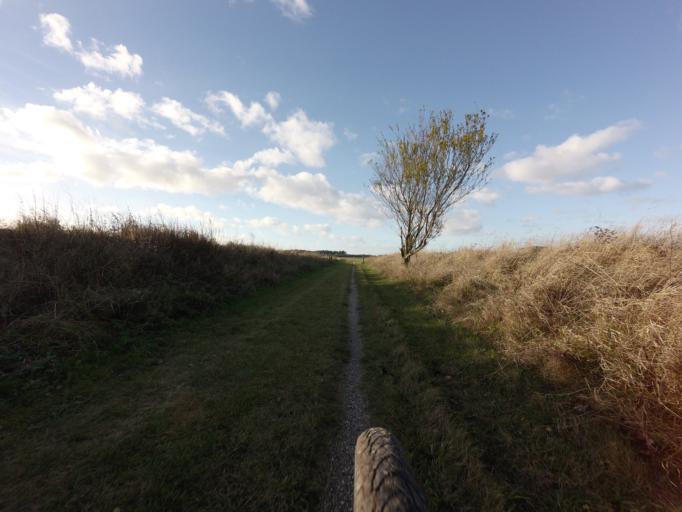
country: DK
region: Central Jutland
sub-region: Syddjurs Kommune
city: Ryomgard
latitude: 56.4929
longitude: 10.6699
